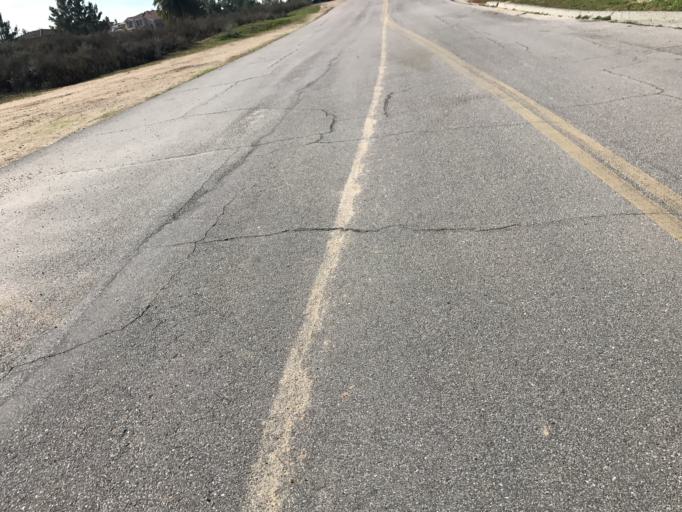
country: US
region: California
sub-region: San Bernardino County
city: Yucaipa
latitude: 34.0438
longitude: -117.0581
